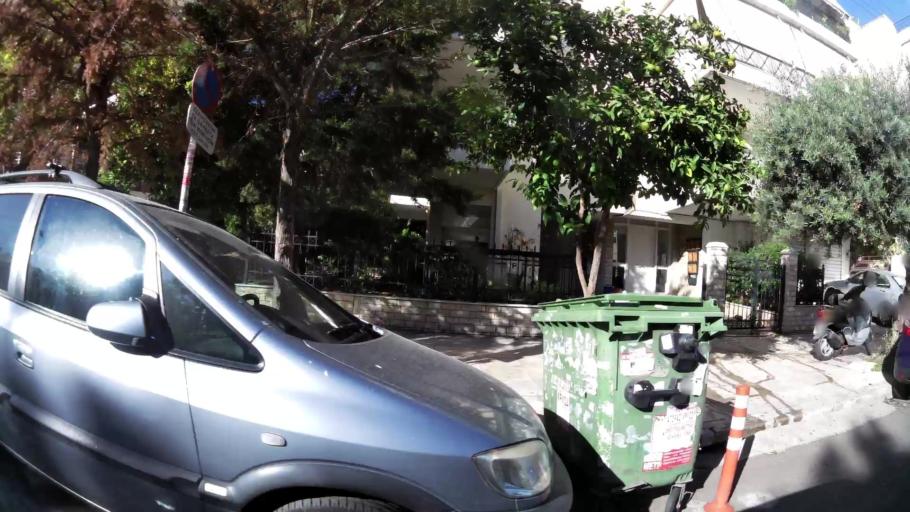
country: GR
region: Attica
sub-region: Nomos Piraios
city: Agios Ioannis Rentis
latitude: 37.9715
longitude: 23.6613
